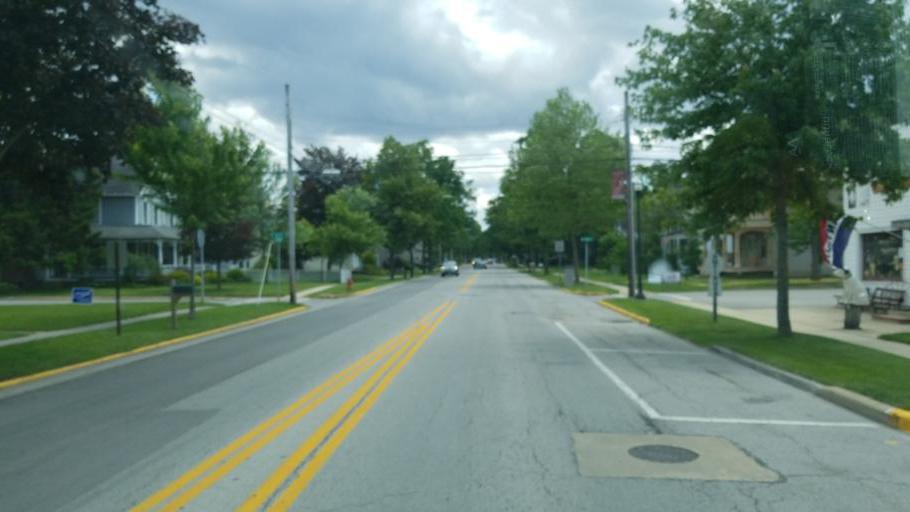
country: US
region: Ohio
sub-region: Erie County
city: Milan
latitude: 41.2971
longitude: -82.6054
